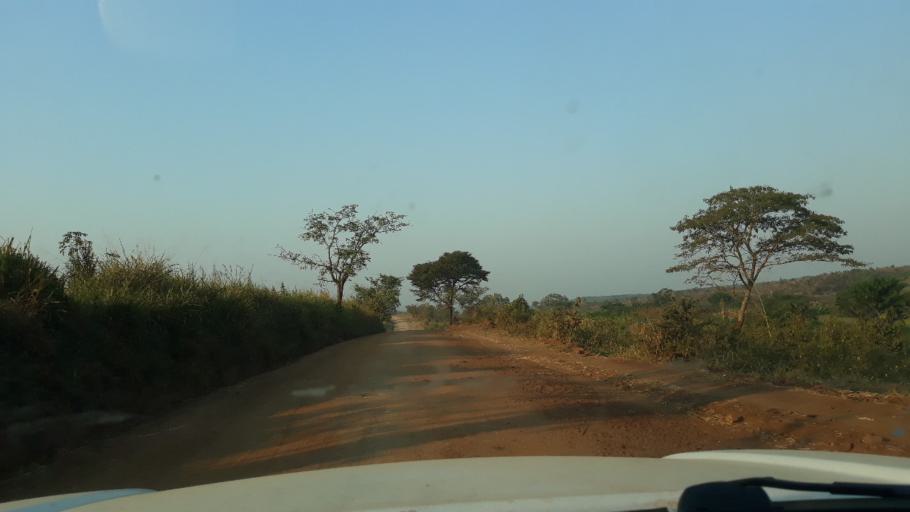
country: BI
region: Bururi
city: Rumonge
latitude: -4.2070
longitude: 29.0138
